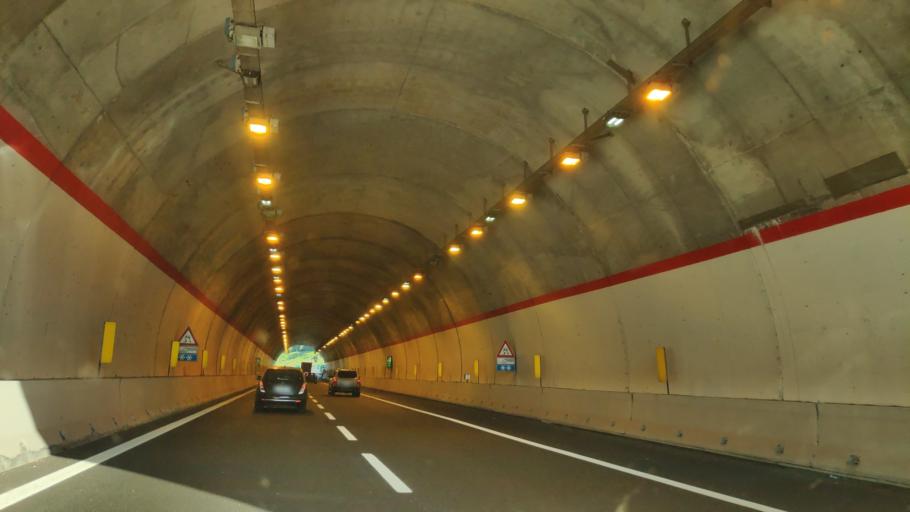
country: IT
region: Basilicate
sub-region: Provincia di Potenza
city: Lagonegro
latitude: 40.1258
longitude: 15.7784
